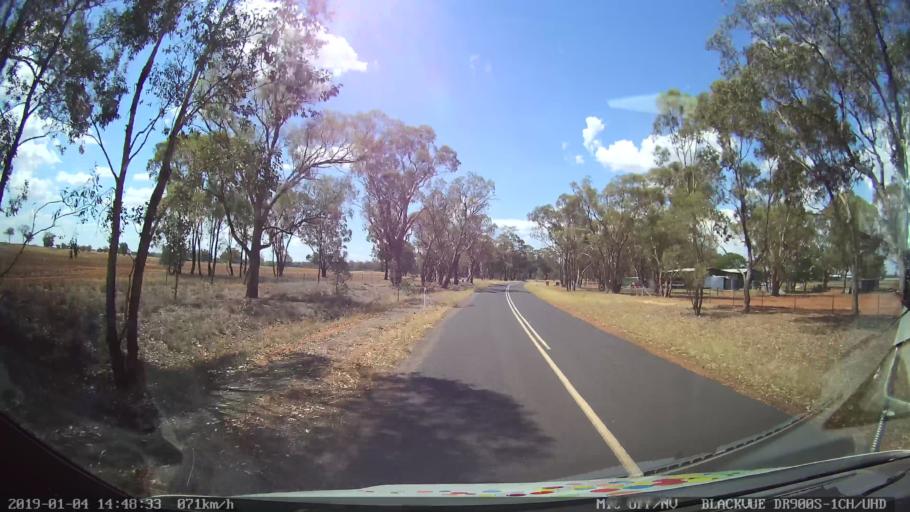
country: AU
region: New South Wales
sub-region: Dubbo Municipality
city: Dubbo
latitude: -32.0579
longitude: 148.6635
